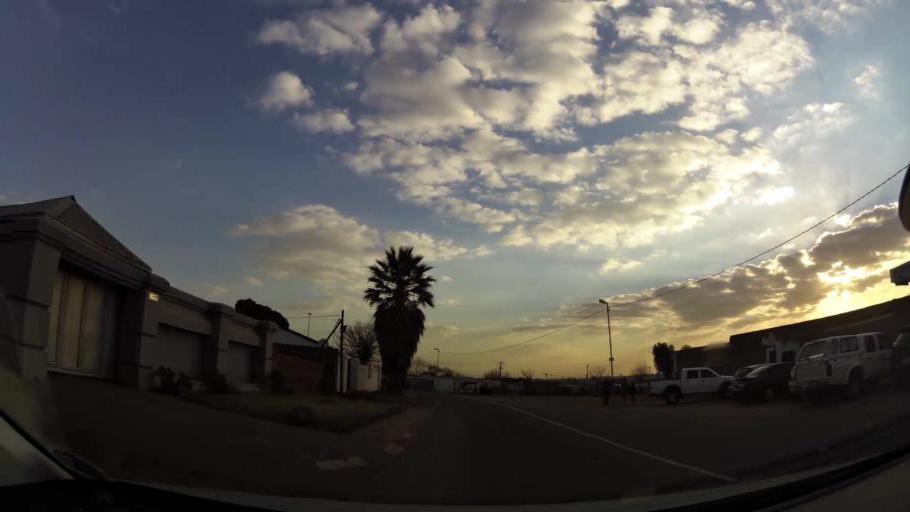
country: ZA
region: Gauteng
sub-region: City of Johannesburg Metropolitan Municipality
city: Soweto
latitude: -26.2627
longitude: 27.8989
